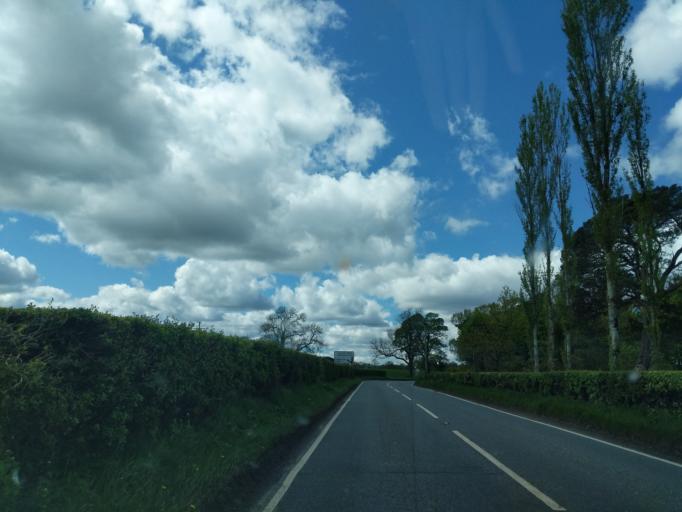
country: GB
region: Scotland
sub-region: Stirling
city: Doune
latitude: 56.1648
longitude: -4.0809
